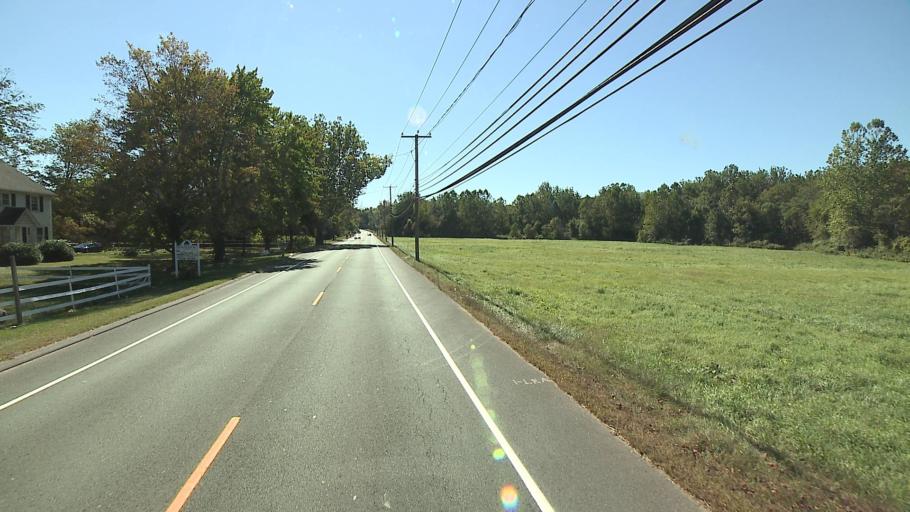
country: US
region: Connecticut
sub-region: Hartford County
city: Salmon Brook
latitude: 41.9441
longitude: -72.7916
